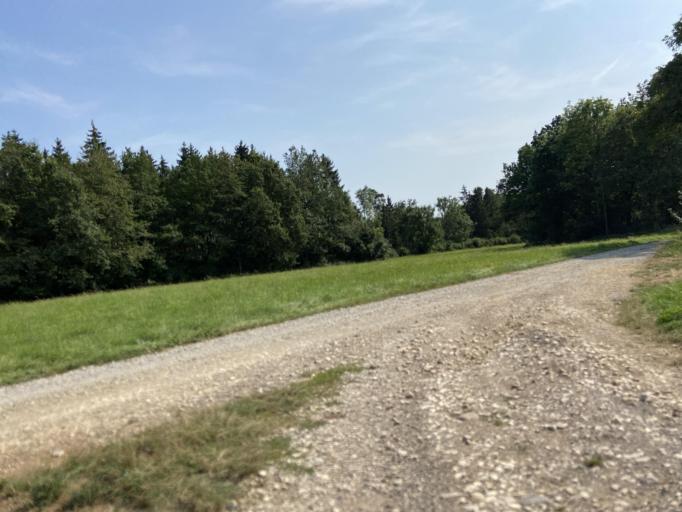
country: DE
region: Baden-Wuerttemberg
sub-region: Tuebingen Region
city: Scheer
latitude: 48.0746
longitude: 9.2788
